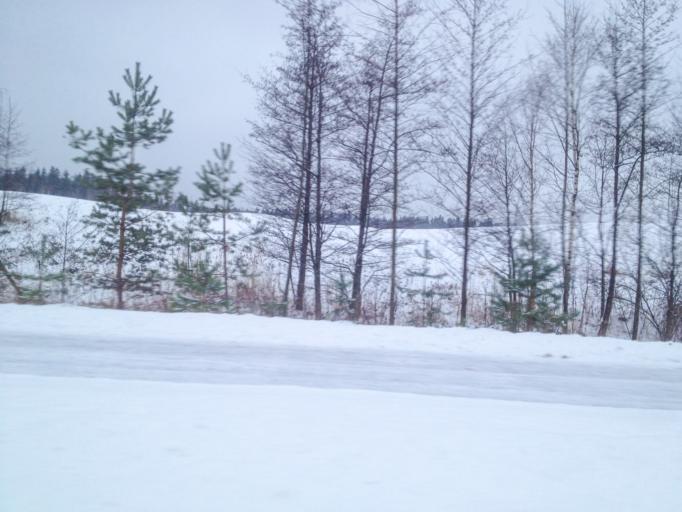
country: FI
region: Uusimaa
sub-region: Helsinki
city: Vantaa
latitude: 60.2092
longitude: 25.1745
